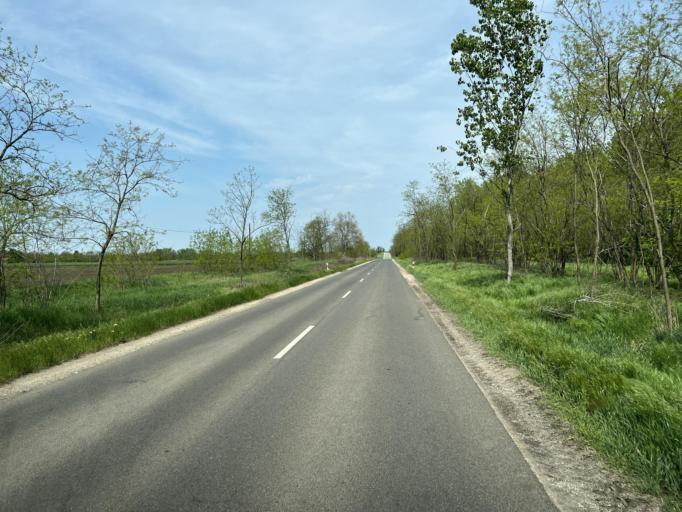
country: HU
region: Pest
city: Abony
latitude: 47.2096
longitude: 19.9865
